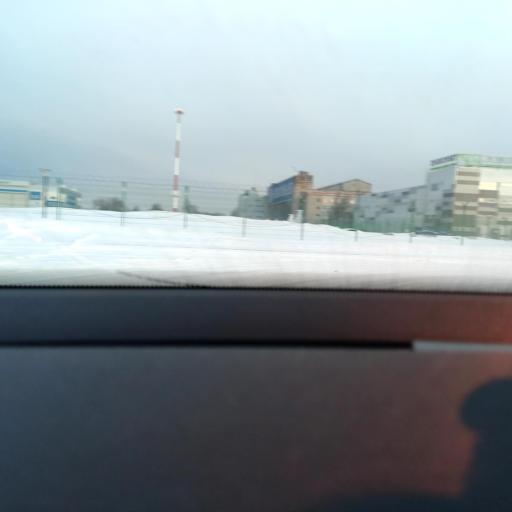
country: RU
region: Moskovskaya
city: Zhukovskiy
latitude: 55.5594
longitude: 38.1201
